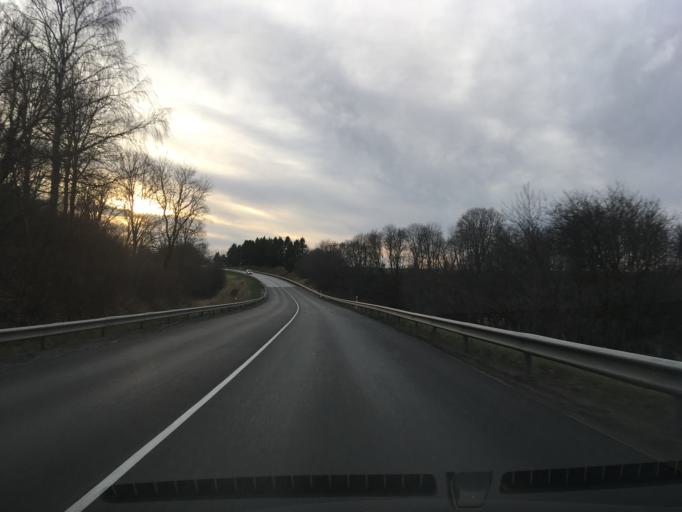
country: EE
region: Ida-Virumaa
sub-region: Aseri vald
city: Aseri
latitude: 59.4351
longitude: 26.7102
